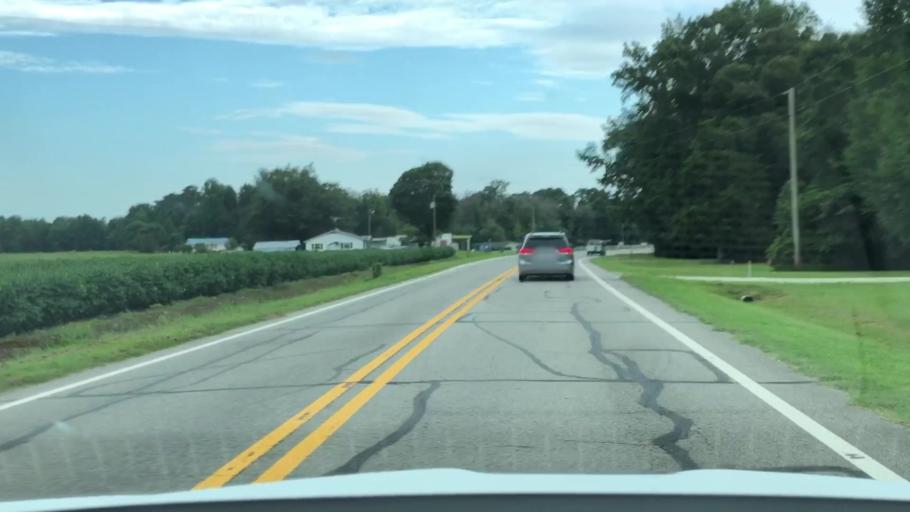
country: US
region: North Carolina
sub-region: Lenoir County
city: Kinston
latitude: 35.1565
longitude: -77.5514
